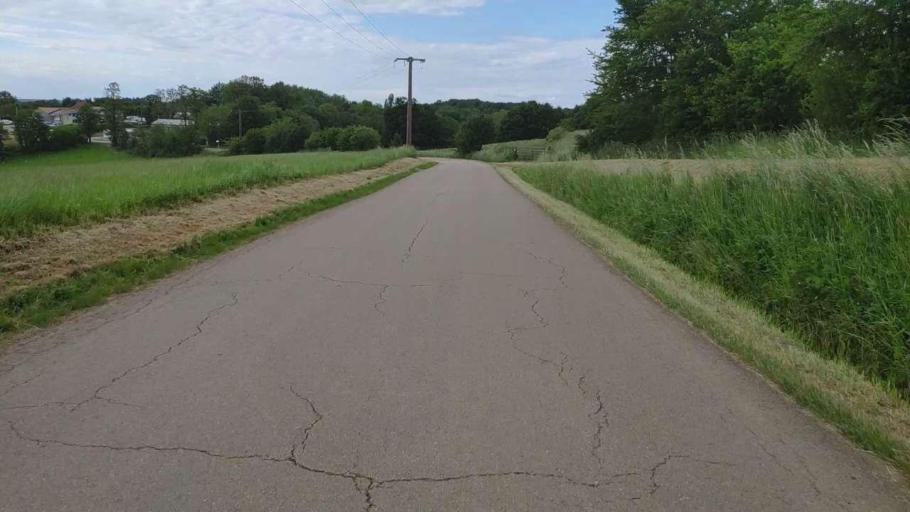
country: FR
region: Franche-Comte
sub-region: Departement du Jura
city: Bletterans
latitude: 46.7970
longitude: 5.5542
